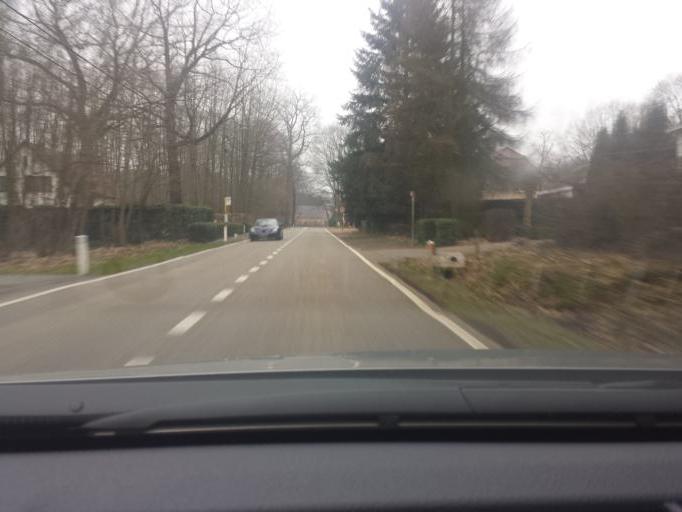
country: BE
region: Flanders
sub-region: Provincie Limburg
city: Lummen
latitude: 50.9875
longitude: 5.1719
